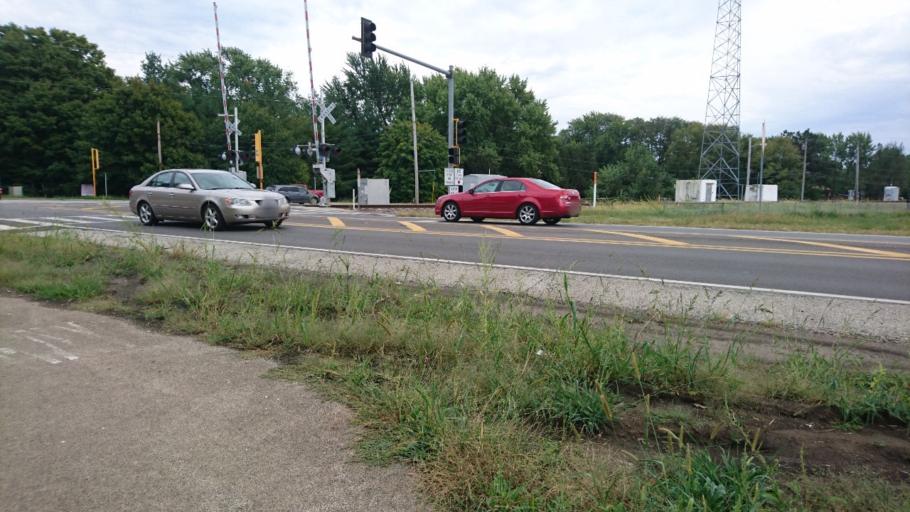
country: US
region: Illinois
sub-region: Sangamon County
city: Southern View
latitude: 39.7205
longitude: -89.6797
